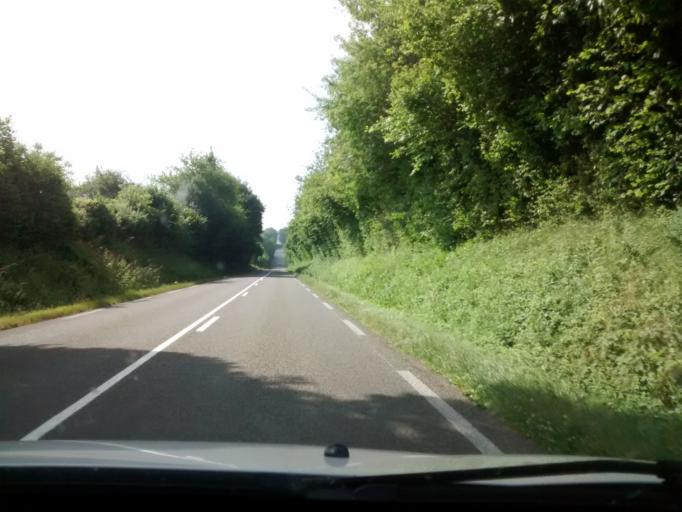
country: FR
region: Pays de la Loire
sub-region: Departement de la Sarthe
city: Cherre
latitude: 48.1371
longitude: 0.6945
